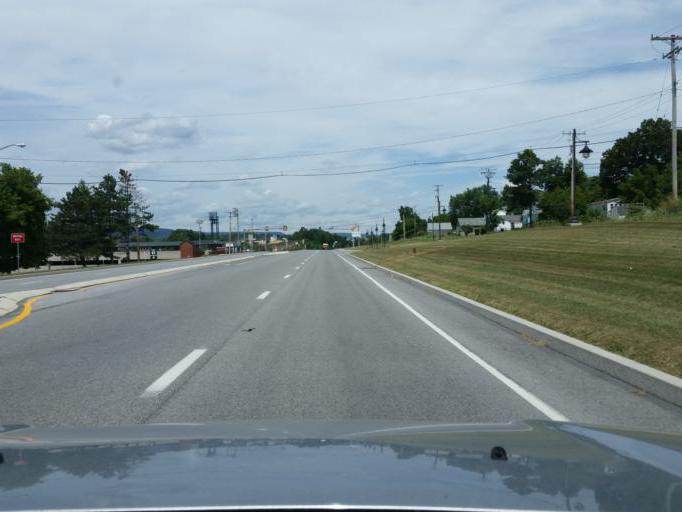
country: US
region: Pennsylvania
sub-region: Blair County
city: Lakemont
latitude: 40.4703
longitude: -78.3927
